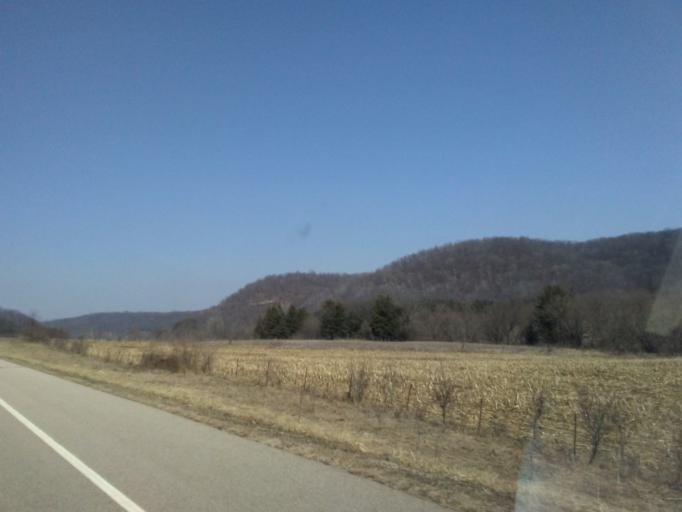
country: US
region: Wisconsin
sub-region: Richland County
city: Richland Center
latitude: 43.3555
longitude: -90.5548
